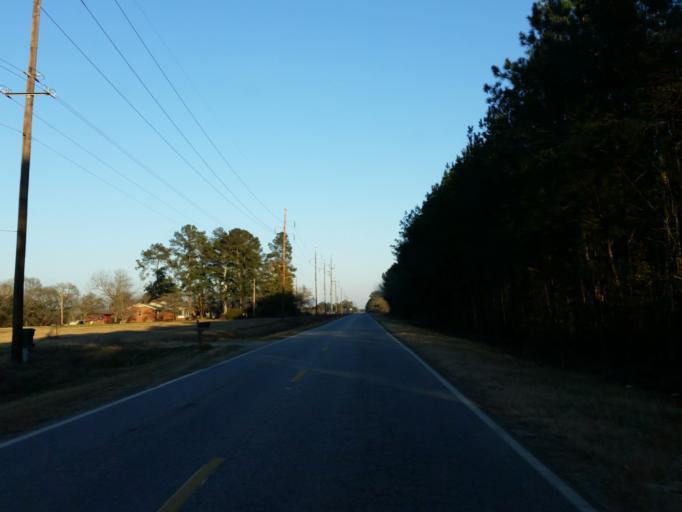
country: US
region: Georgia
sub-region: Crisp County
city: Cordele
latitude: 32.0043
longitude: -83.7887
